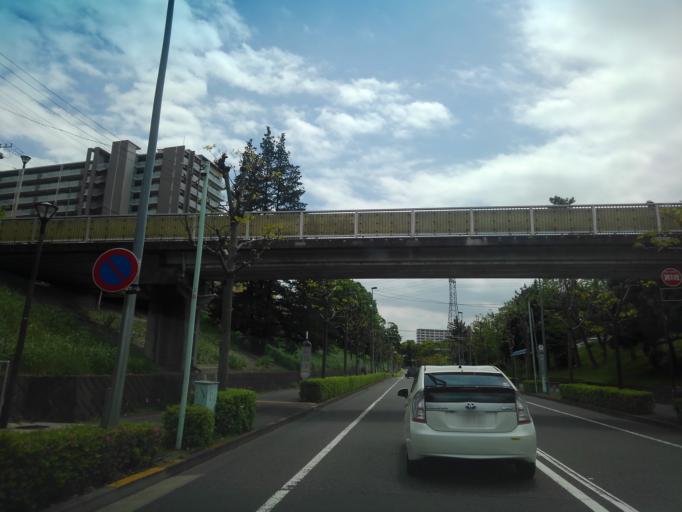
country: JP
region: Tokyo
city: Hino
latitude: 35.6259
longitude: 139.4496
